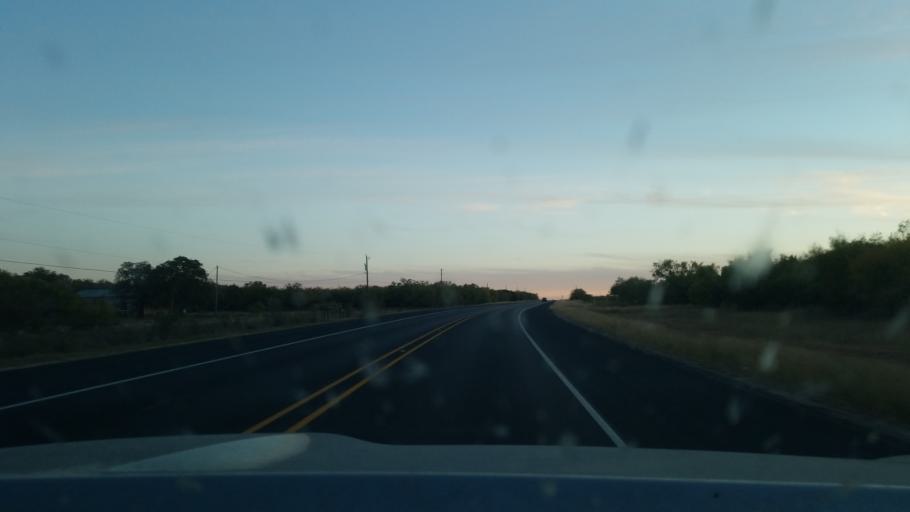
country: US
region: Texas
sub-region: Stephens County
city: Breckenridge
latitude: 32.6105
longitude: -98.9000
